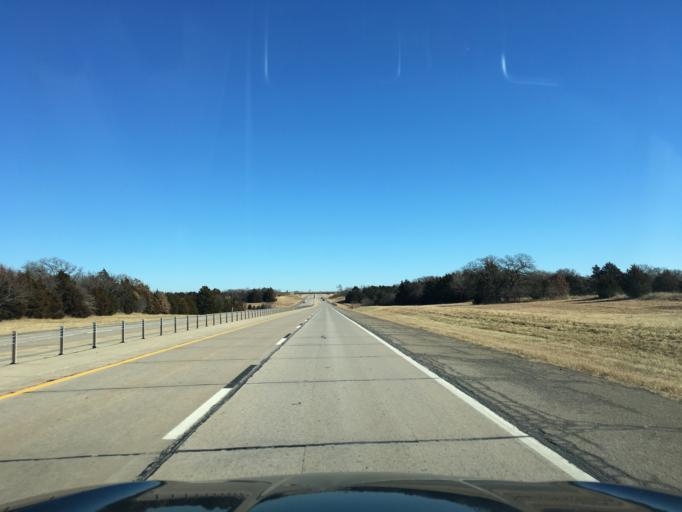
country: US
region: Oklahoma
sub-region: Pawnee County
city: Pawnee
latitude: 36.2248
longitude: -96.8267
